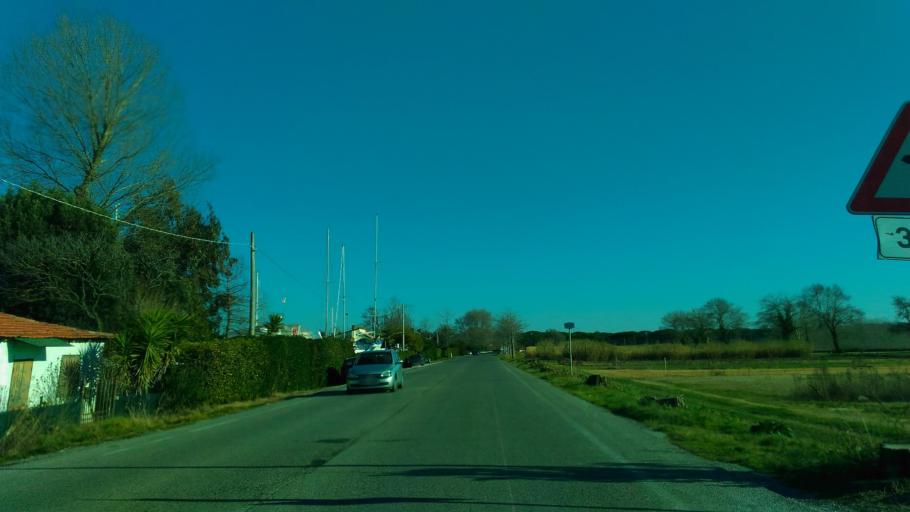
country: IT
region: Tuscany
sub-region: Province of Pisa
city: Marina di Pisa
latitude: 43.6761
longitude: 10.3136
